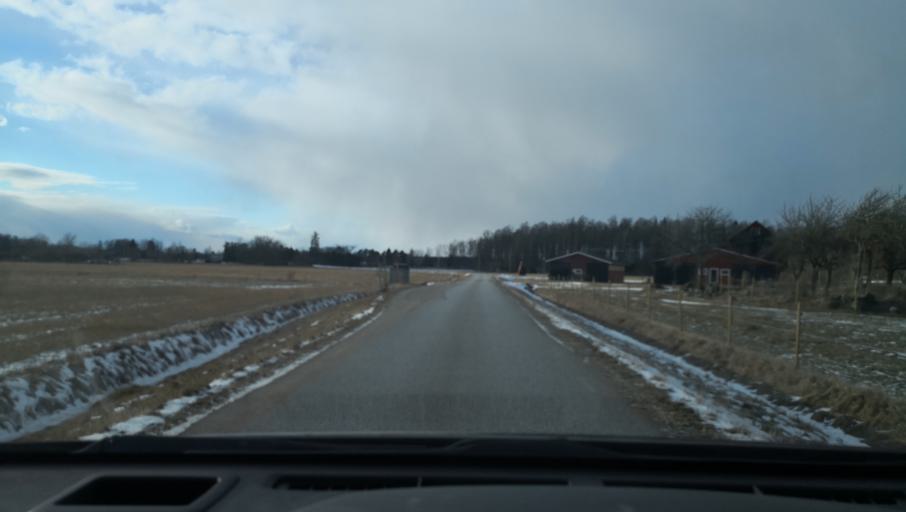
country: SE
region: Uppsala
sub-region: Enkopings Kommun
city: Irsta
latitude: 59.7011
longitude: 16.9404
